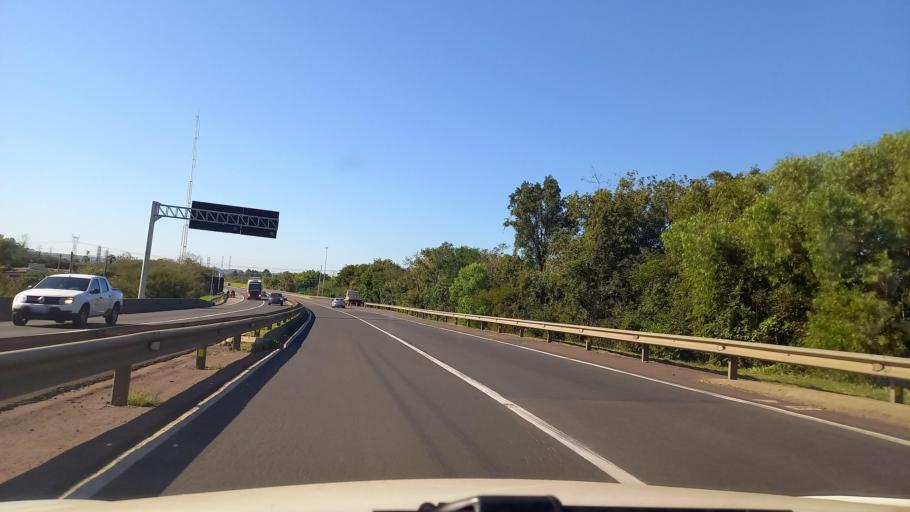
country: BR
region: Rio Grande do Sul
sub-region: Portao
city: Portao
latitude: -29.8234
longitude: -51.3493
